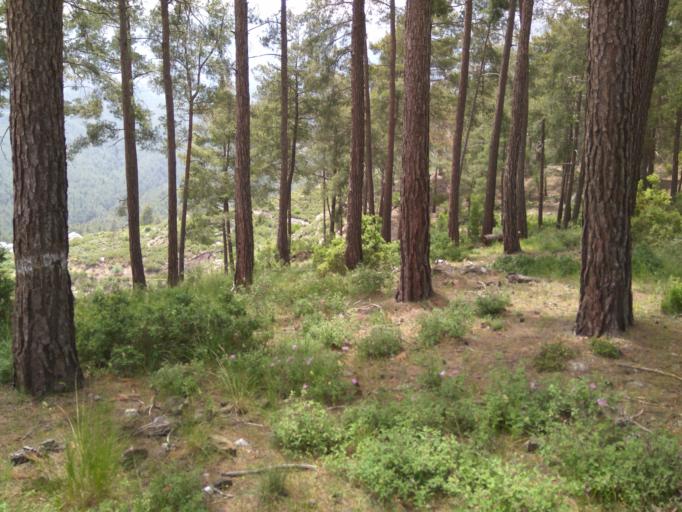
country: TR
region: Antalya
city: Altinyaka
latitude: 36.6036
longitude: 30.4408
